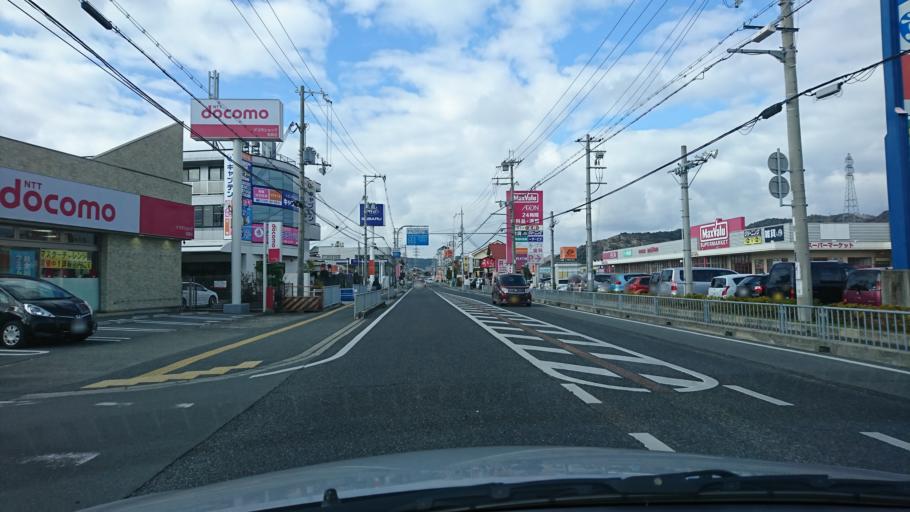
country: JP
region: Hyogo
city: Kakogawacho-honmachi
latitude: 34.7856
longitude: 134.8069
